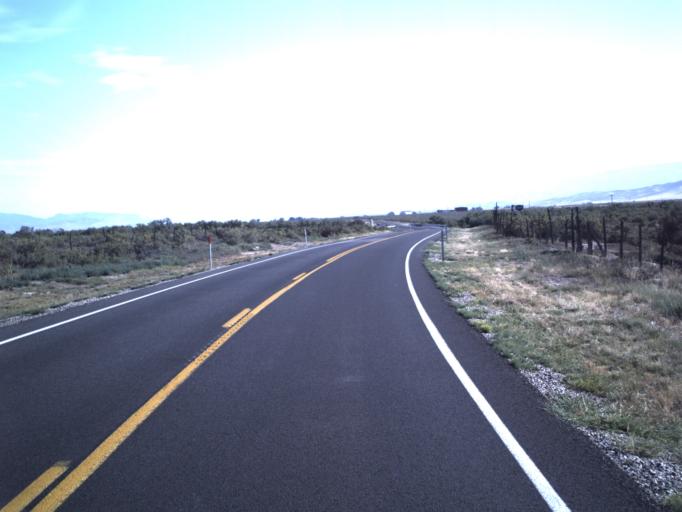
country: US
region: Utah
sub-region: Sevier County
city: Salina
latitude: 39.0185
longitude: -111.8512
